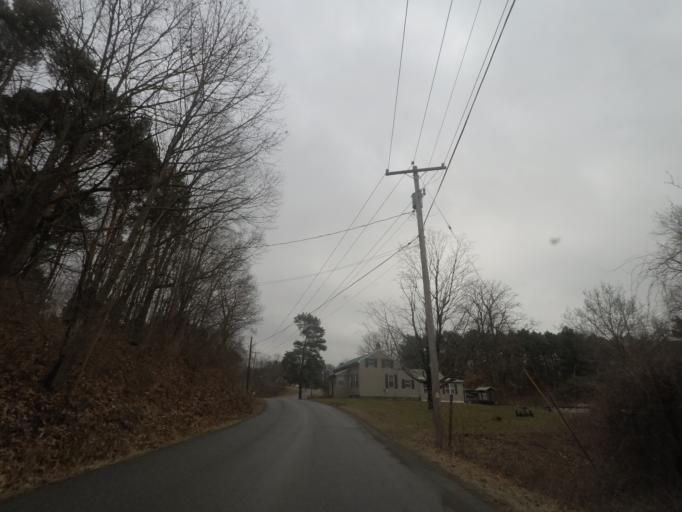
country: US
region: New York
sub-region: Saratoga County
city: Waterford
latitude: 42.7706
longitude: -73.6406
